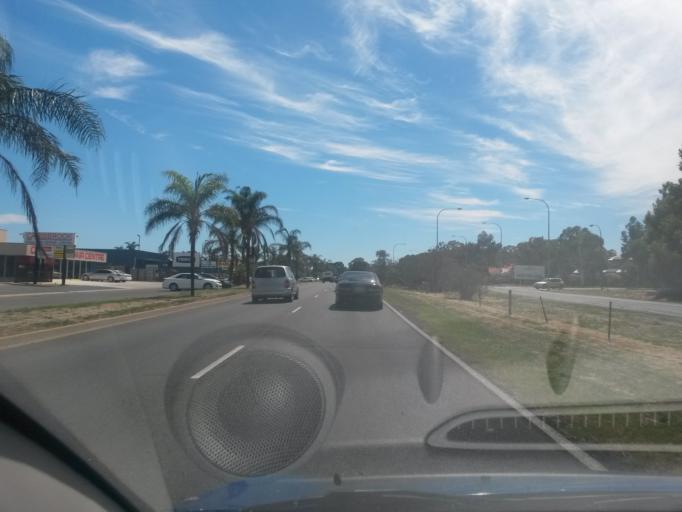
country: AU
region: South Australia
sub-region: Salisbury
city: Salisbury
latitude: -34.7716
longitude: 138.6646
